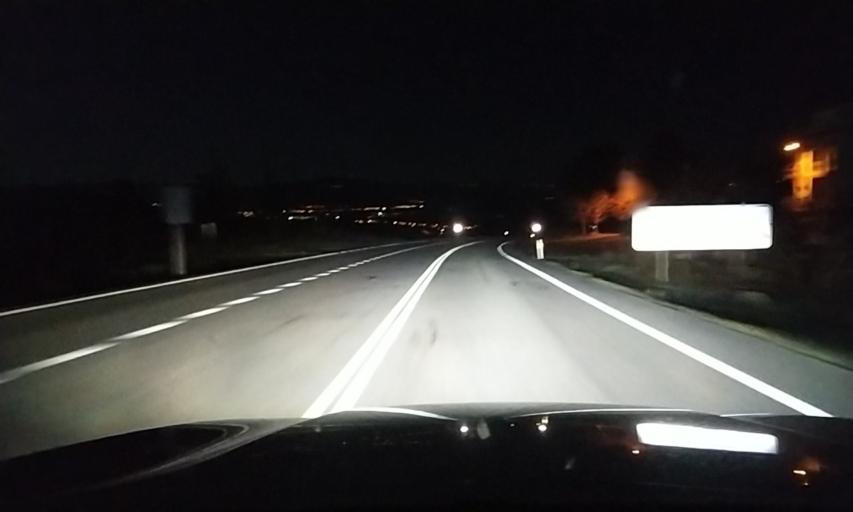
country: ES
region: Galicia
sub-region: Provincia de Ourense
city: Cualedro
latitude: 41.9766
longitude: -7.5214
